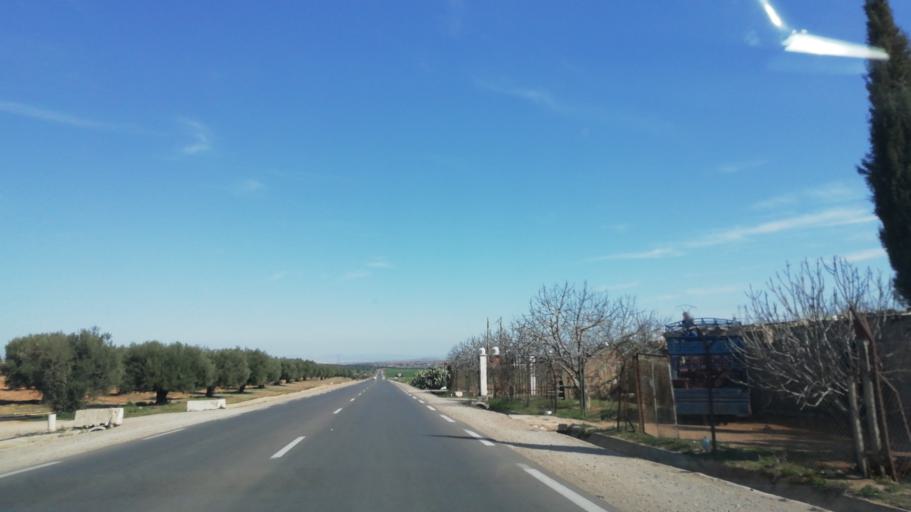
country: DZ
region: Mascara
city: Mascara
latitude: 35.4172
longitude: 0.4054
